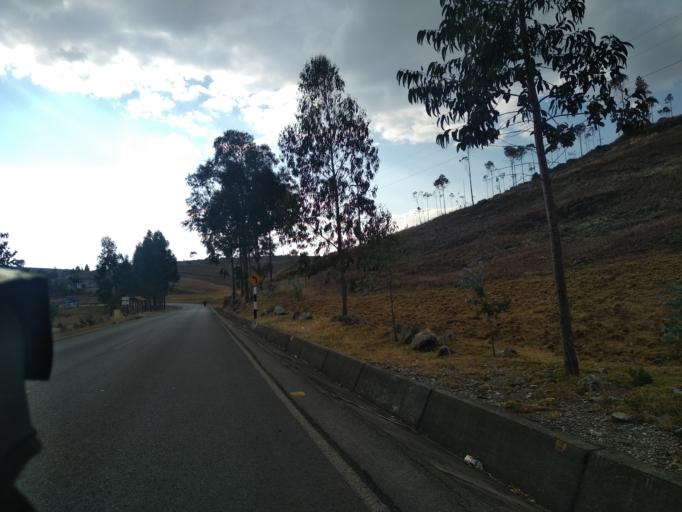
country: PE
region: Cajamarca
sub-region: Provincia de Cajamarca
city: Llacanora
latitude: -7.1443
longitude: -78.4008
